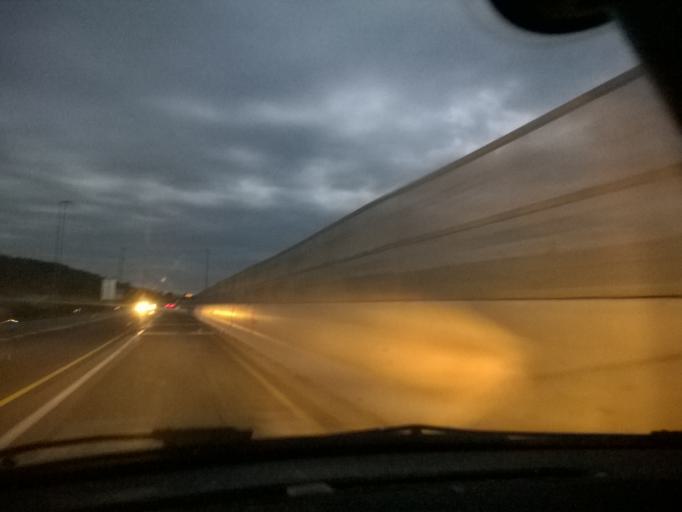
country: SI
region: Podlehnik
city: Podlehnik
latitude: 46.3307
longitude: 15.8781
